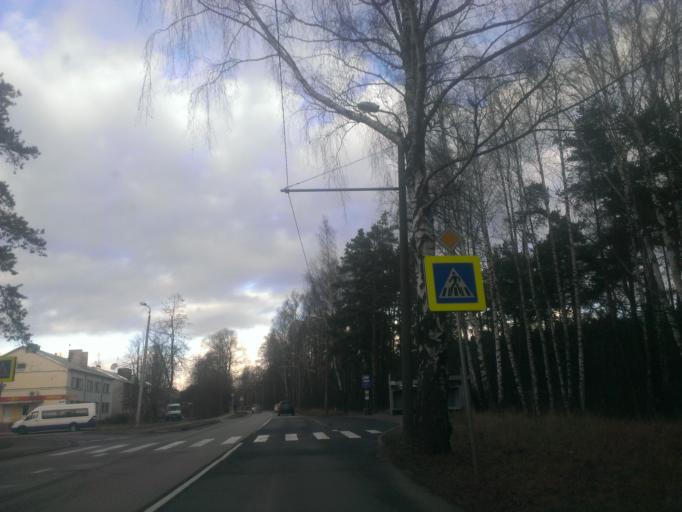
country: LV
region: Riga
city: Bolderaja
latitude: 57.0590
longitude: 24.1058
